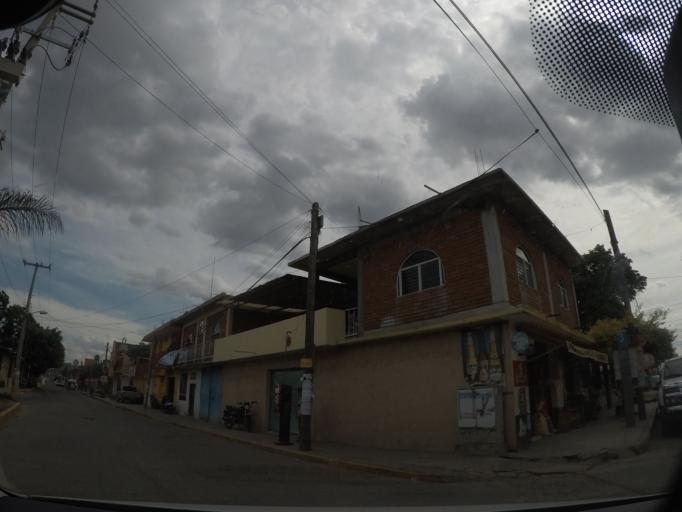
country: MX
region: Oaxaca
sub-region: Santa Cruz Amilpas
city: Santa Cruz Amilpas
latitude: 17.0638
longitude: -96.6814
